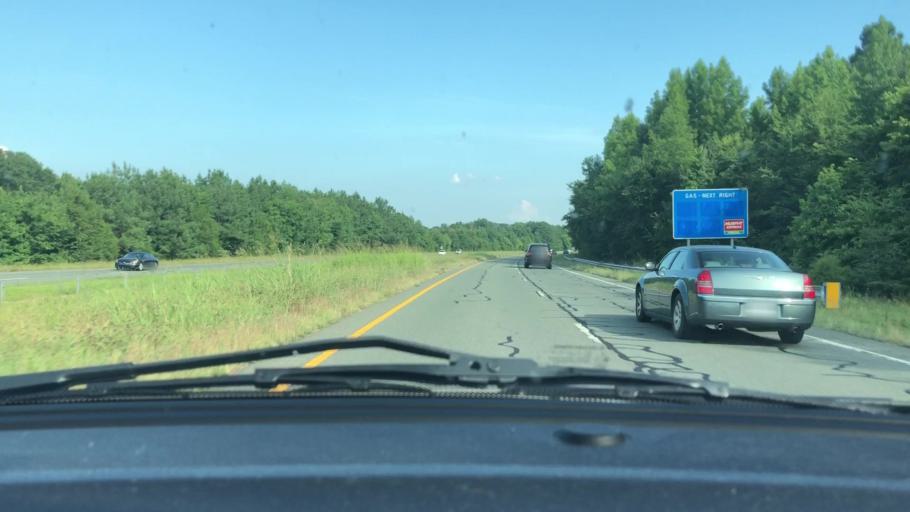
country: US
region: North Carolina
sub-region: Chatham County
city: Siler City
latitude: 35.7422
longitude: -79.4366
